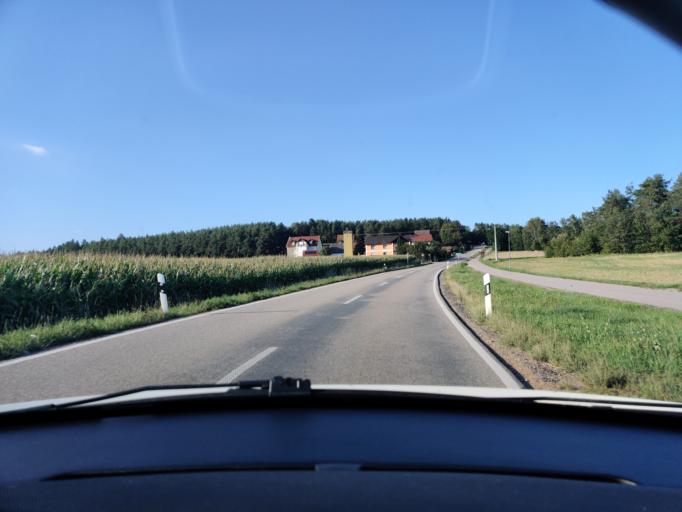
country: DE
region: Bavaria
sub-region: Upper Palatinate
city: Stulln
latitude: 49.4258
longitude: 12.1391
